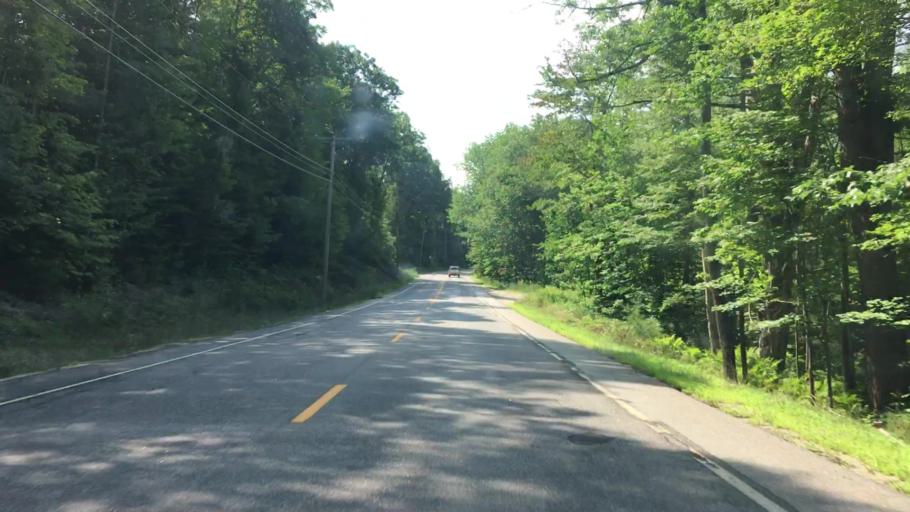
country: US
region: Maine
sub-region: Cumberland County
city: Raymond
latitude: 43.9245
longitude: -70.4359
